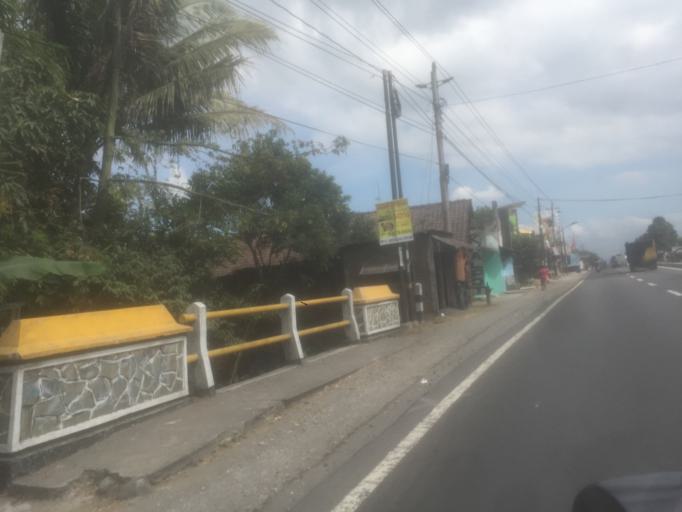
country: ID
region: Central Java
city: Muntilan
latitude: -7.6174
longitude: 110.3092
